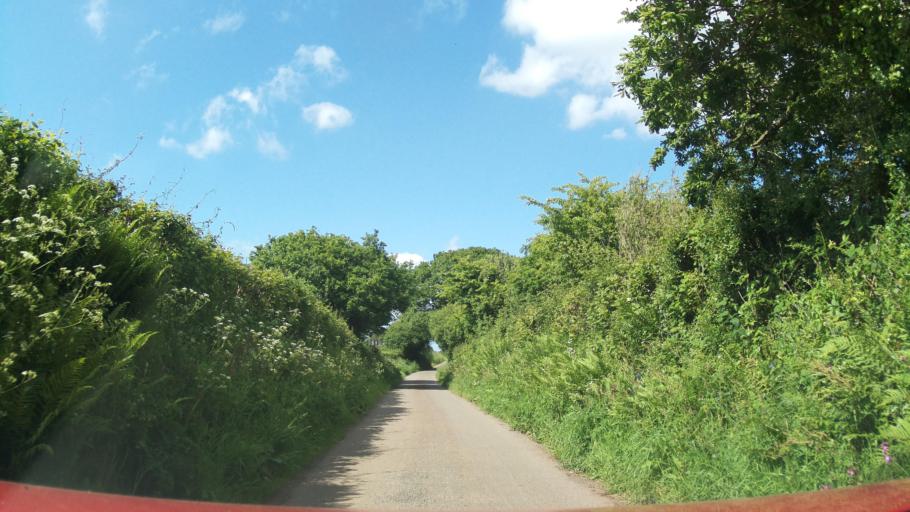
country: GB
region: England
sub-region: Devon
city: Totnes
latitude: 50.4073
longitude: -3.7013
